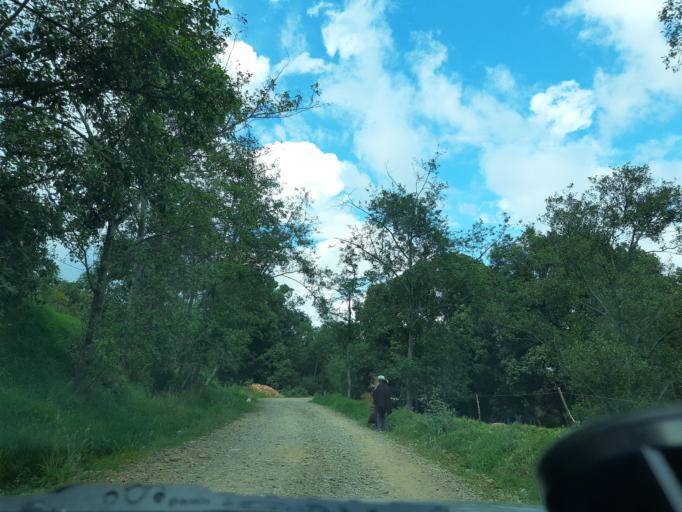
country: CO
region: Boyaca
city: Raquira
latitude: 5.5071
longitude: -73.6698
